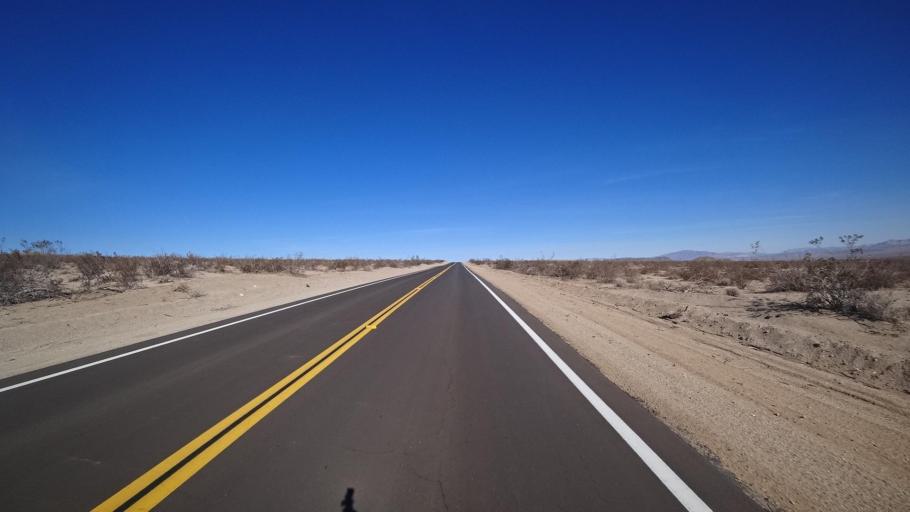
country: US
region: California
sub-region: Kern County
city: Ridgecrest
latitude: 35.5135
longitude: -117.6099
